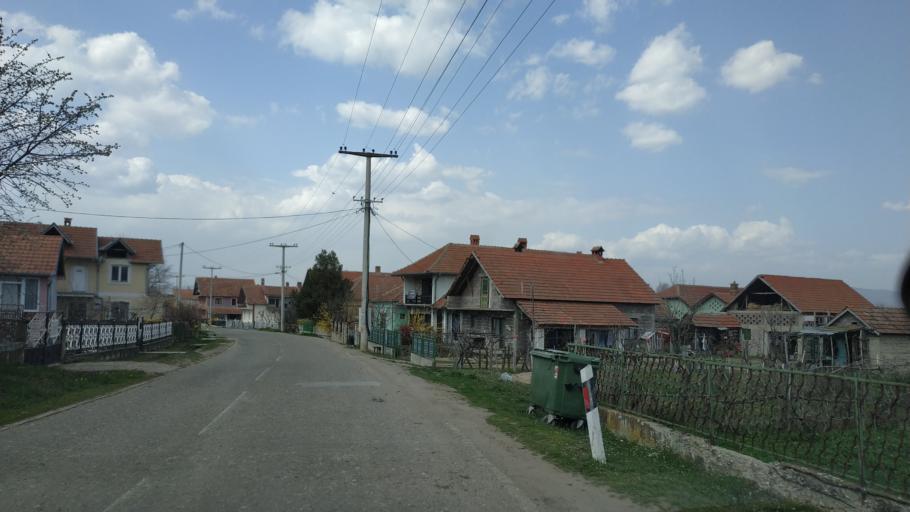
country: RS
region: Central Serbia
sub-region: Nisavski Okrug
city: Aleksinac
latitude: 43.5561
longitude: 21.6103
